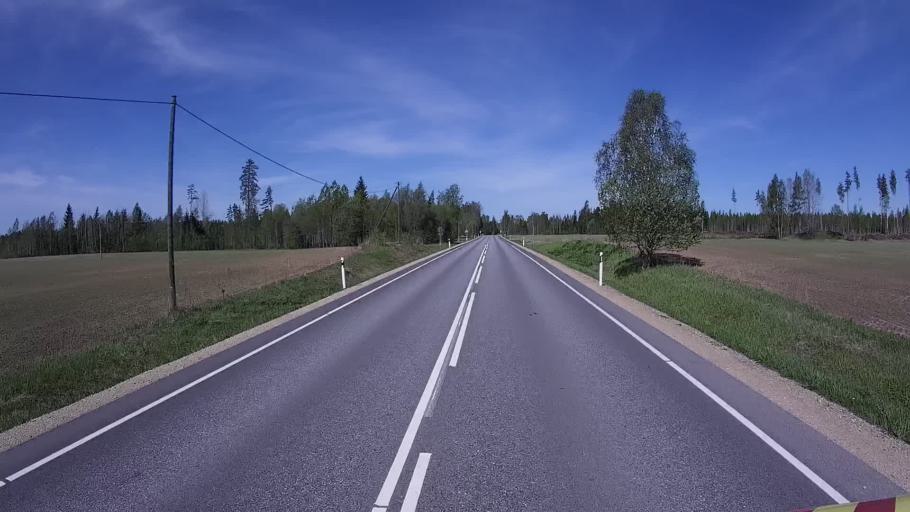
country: EE
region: Polvamaa
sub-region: Raepina vald
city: Rapina
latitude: 57.9785
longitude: 27.2867
